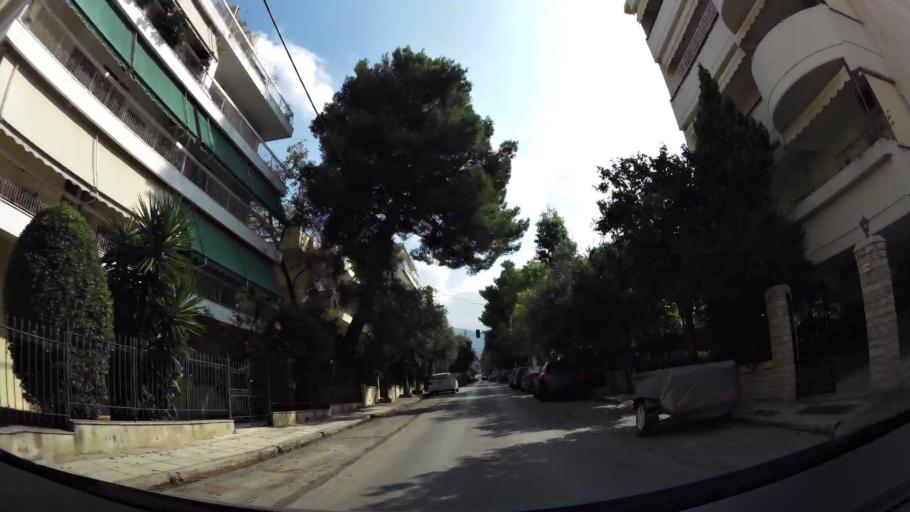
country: GR
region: Attica
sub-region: Nomarchia Athinas
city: Cholargos
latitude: 37.9969
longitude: 23.7962
